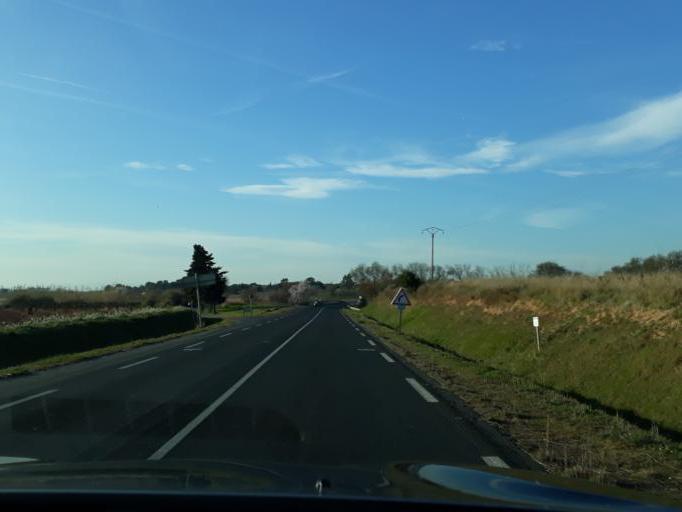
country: FR
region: Languedoc-Roussillon
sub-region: Departement de l'Herault
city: Marseillan
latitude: 43.3286
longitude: 3.5270
